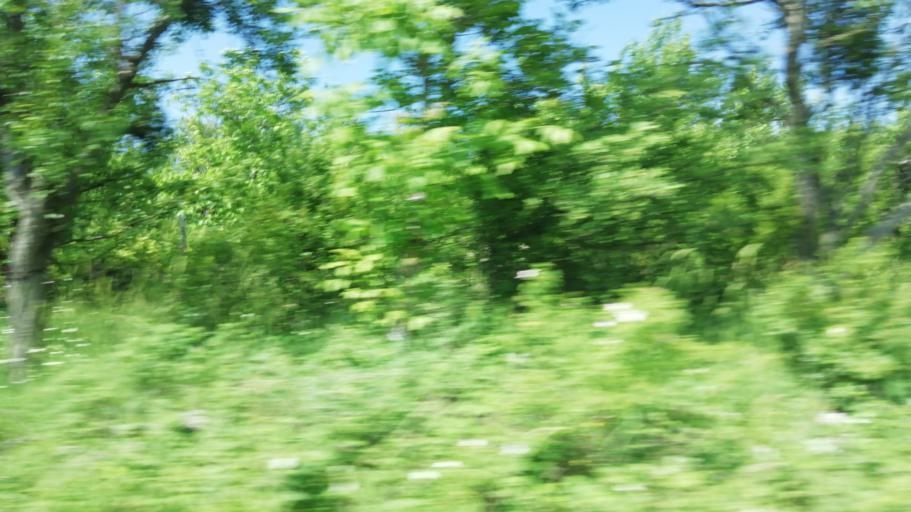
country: TR
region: Karabuk
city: Karabuk
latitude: 41.1250
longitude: 32.5762
